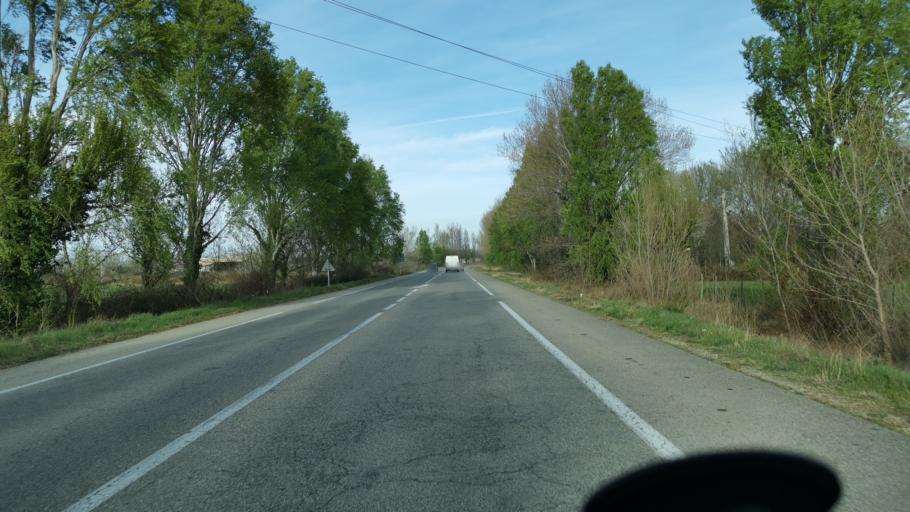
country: FR
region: Provence-Alpes-Cote d'Azur
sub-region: Departement des Bouches-du-Rhone
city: Saint-Martin-de-Crau
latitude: 43.5954
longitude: 4.7635
